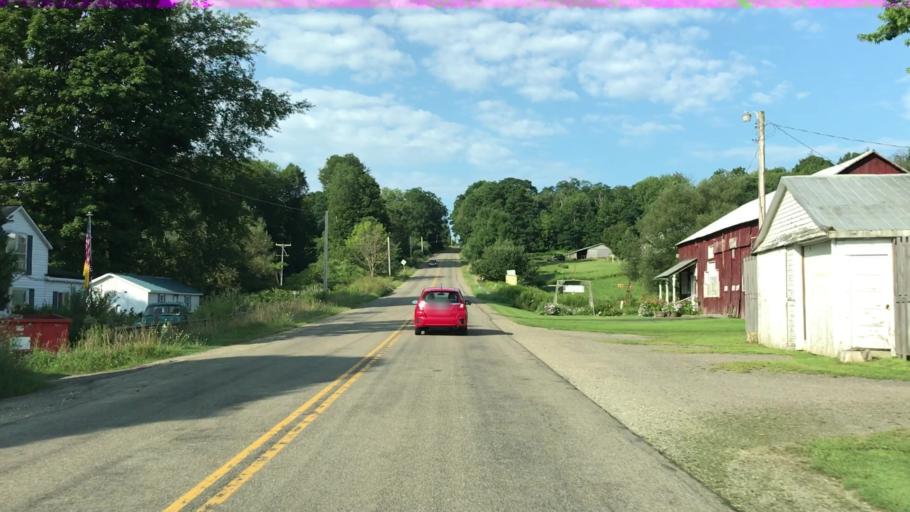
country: US
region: New York
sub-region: Chautauqua County
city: Mayville
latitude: 42.2843
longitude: -79.4360
